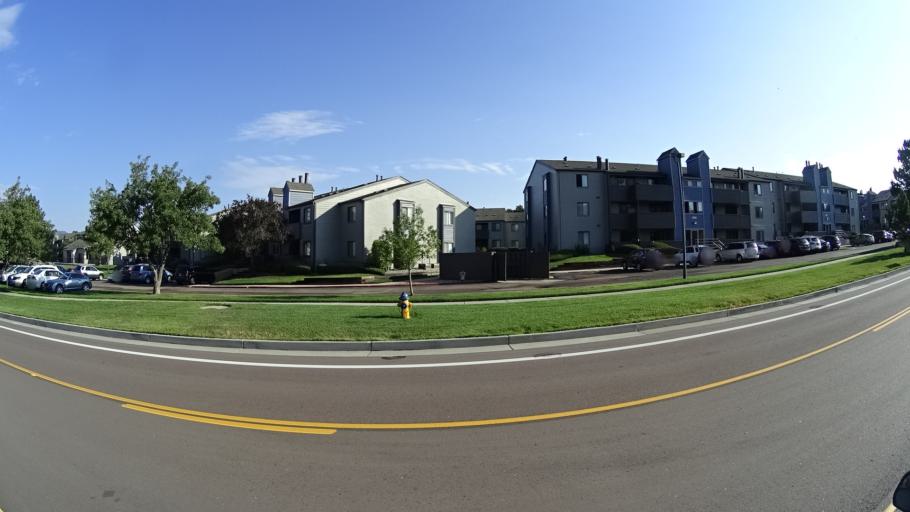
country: US
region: Colorado
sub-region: El Paso County
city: Air Force Academy
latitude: 38.9494
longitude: -104.7860
